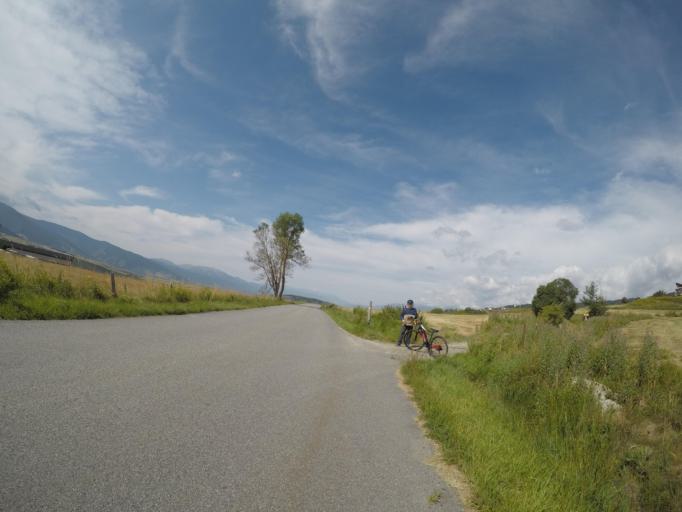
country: ES
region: Catalonia
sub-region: Provincia de Girona
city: Llivia
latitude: 42.5017
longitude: 2.0705
